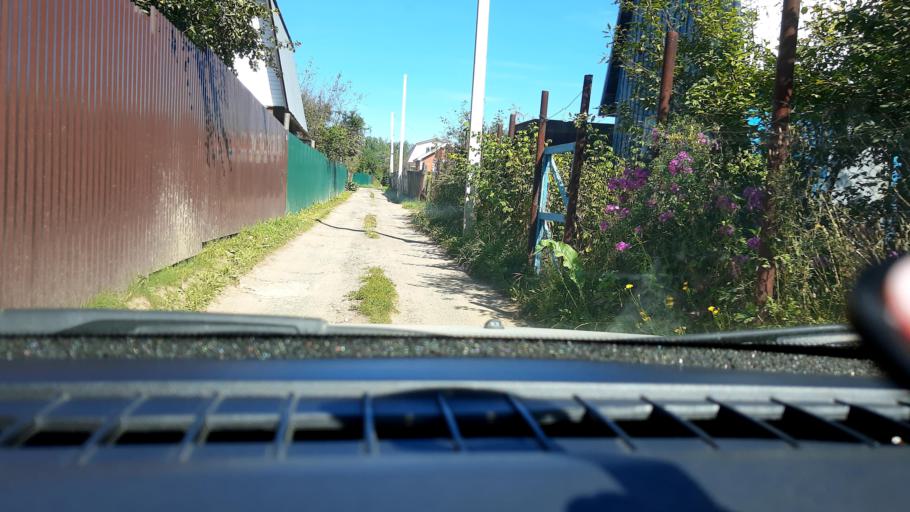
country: RU
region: Nizjnij Novgorod
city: Afonino
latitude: 56.2087
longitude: 44.1250
